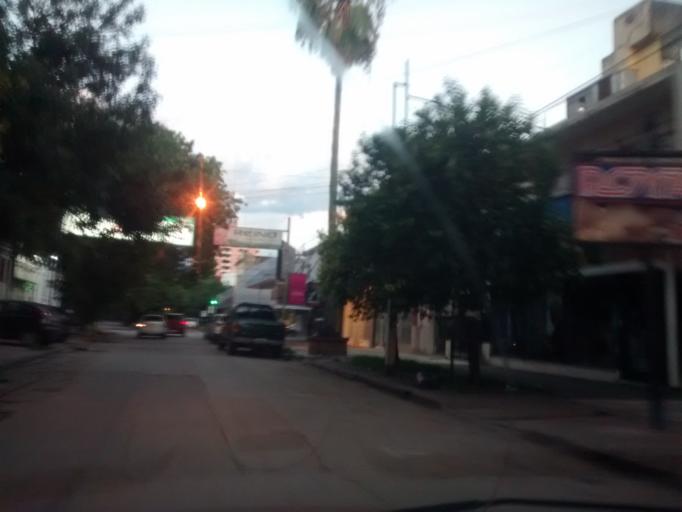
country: AR
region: Chaco
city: Resistencia
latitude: -27.4554
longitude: -58.9861
